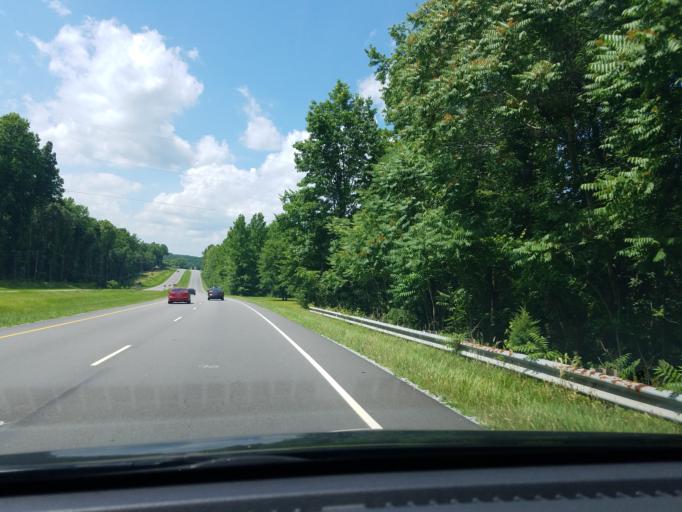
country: US
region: North Carolina
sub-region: Durham County
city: Gorman
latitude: 36.1270
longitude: -78.9012
